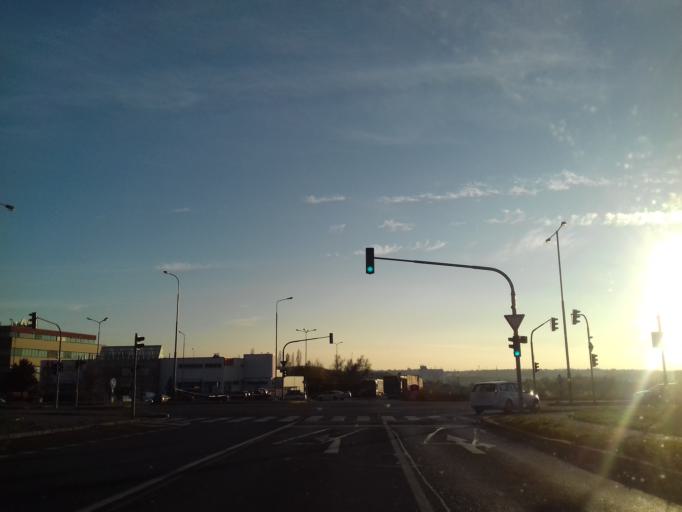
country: CZ
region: Central Bohemia
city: Hostivice
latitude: 50.0442
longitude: 14.3151
